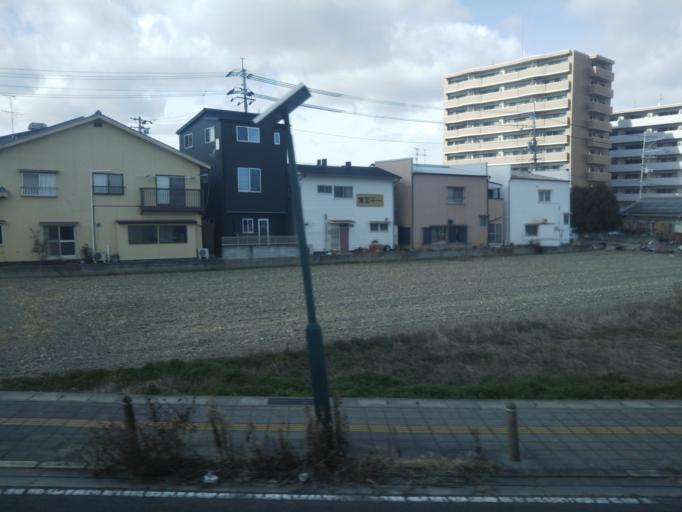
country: JP
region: Okayama
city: Okayama-shi
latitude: 34.6285
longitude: 133.8968
